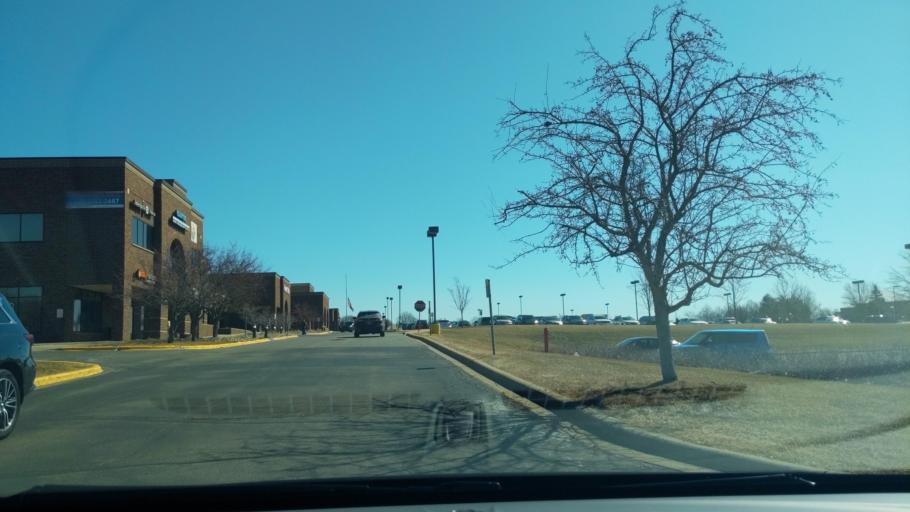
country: US
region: Minnesota
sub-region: Carver County
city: Chanhassen
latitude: 44.8633
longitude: -93.5438
